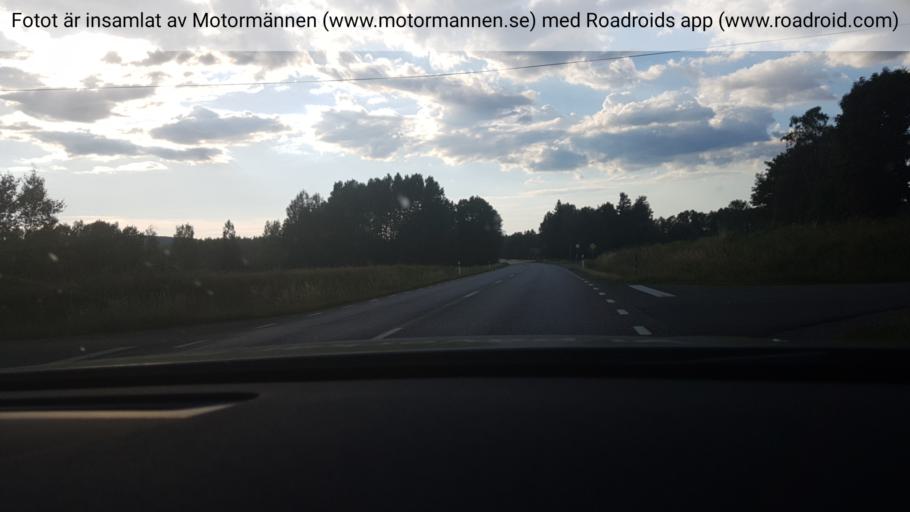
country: SE
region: Vaestra Goetaland
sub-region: Tidaholms Kommun
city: Tidaholm
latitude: 58.2039
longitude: 13.8829
